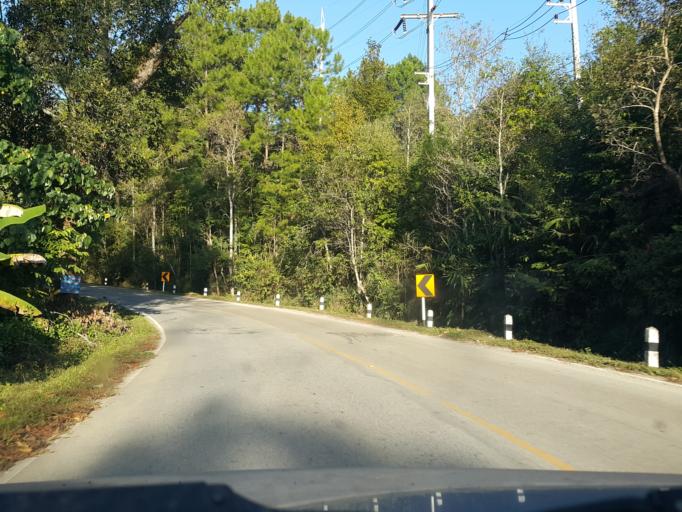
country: TH
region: Mae Hong Son
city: Mae Hi
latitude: 19.2671
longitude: 98.5900
